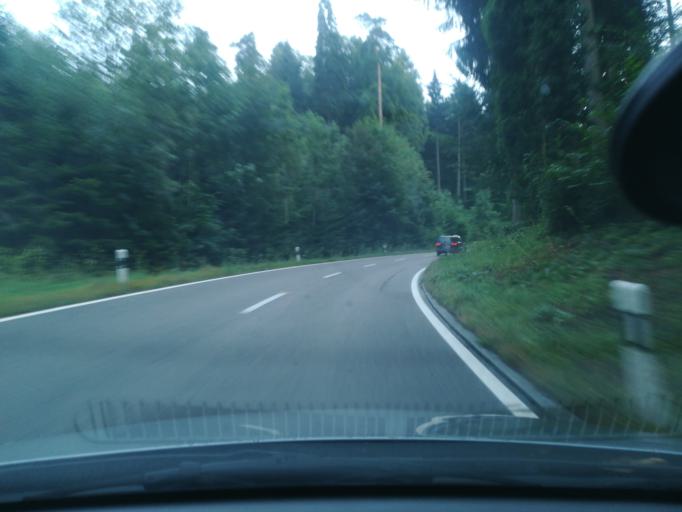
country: CH
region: Thurgau
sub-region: Frauenfeld District
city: Huttwilen
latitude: 47.6192
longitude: 8.8843
